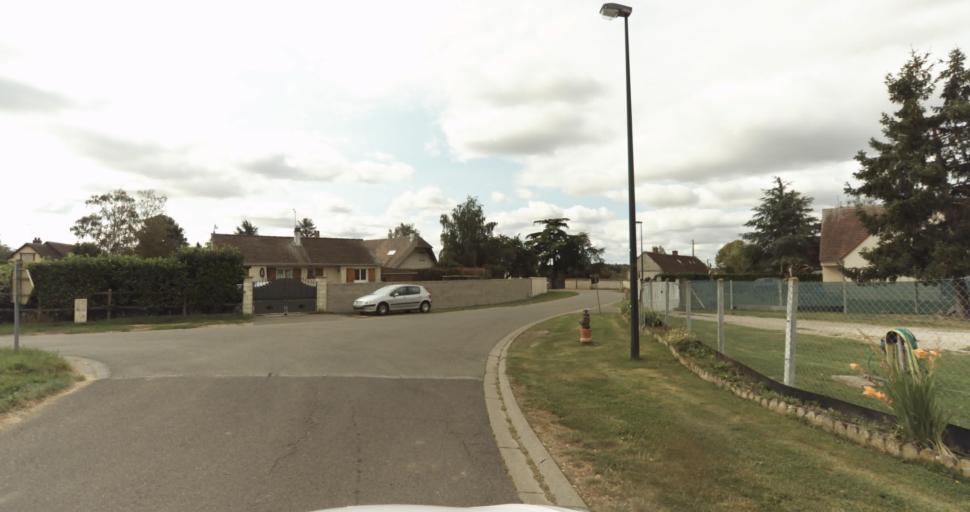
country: FR
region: Haute-Normandie
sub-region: Departement de l'Eure
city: Tillieres-sur-Avre
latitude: 48.7817
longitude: 1.1035
